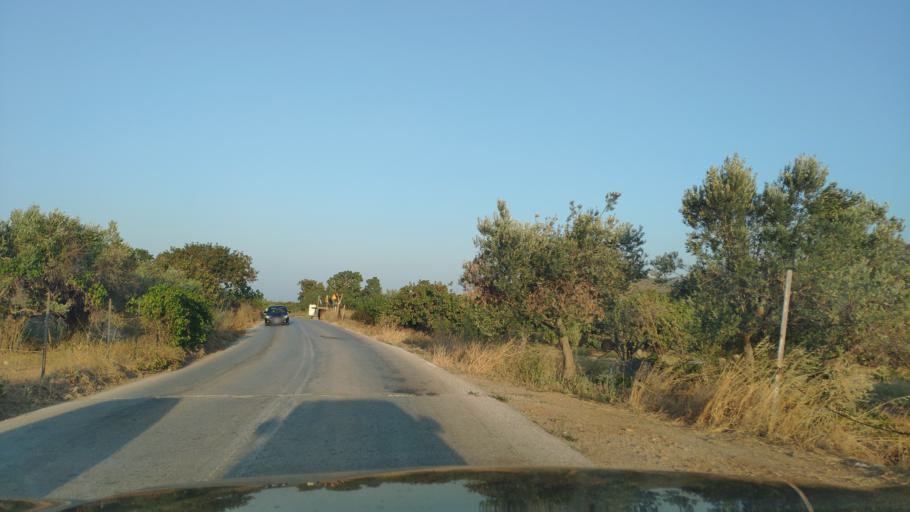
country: GR
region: Attica
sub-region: Nomarchia Anatolikis Attikis
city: Limin Mesoyaias
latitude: 37.9261
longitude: 23.9875
